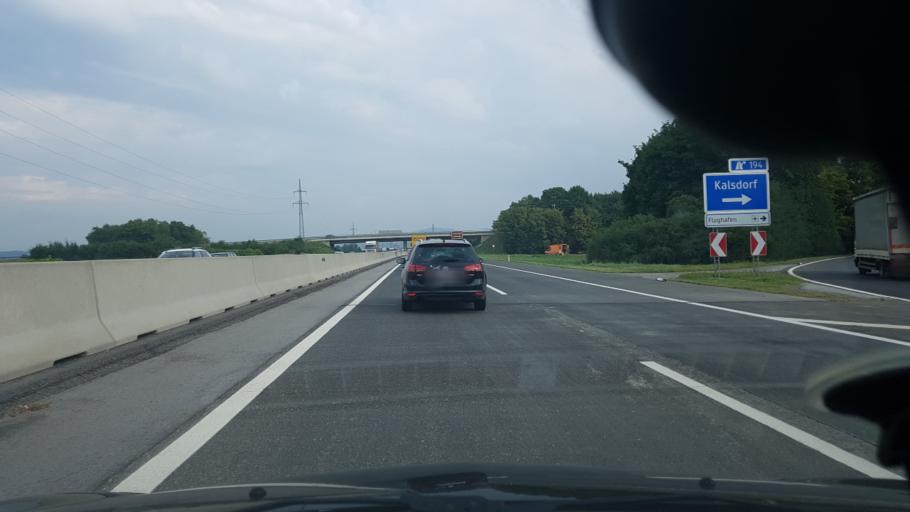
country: AT
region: Styria
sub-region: Politischer Bezirk Graz-Umgebung
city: Zettling
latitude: 46.9610
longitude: 15.4389
